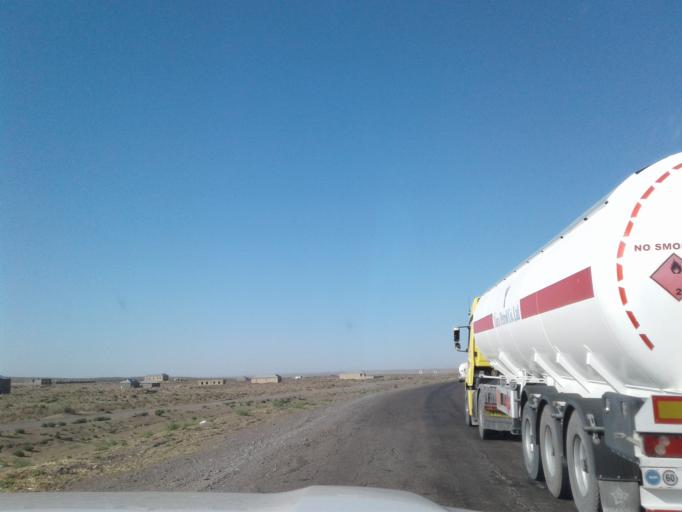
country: TM
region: Mary
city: Yoloeten
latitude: 36.7671
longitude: 62.4797
